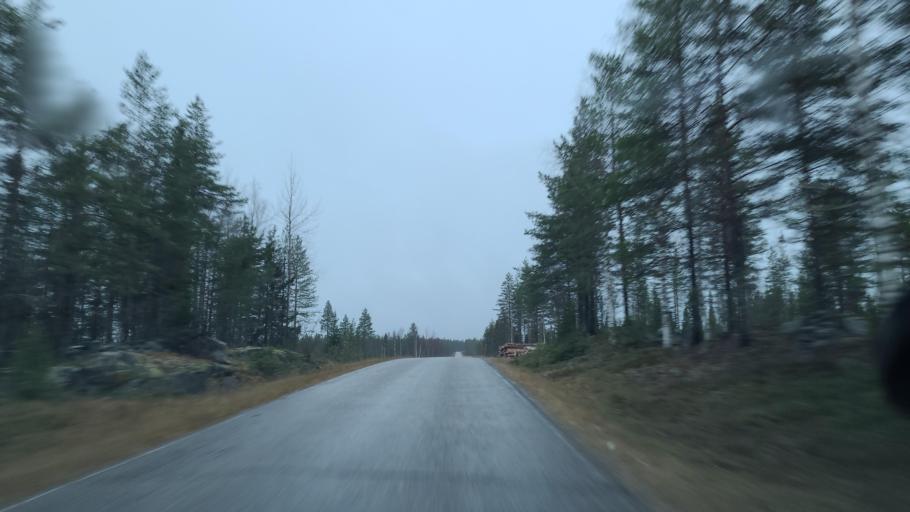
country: FI
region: Lapland
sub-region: Kemi-Tornio
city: Simo
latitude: 65.9101
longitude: 25.2025
